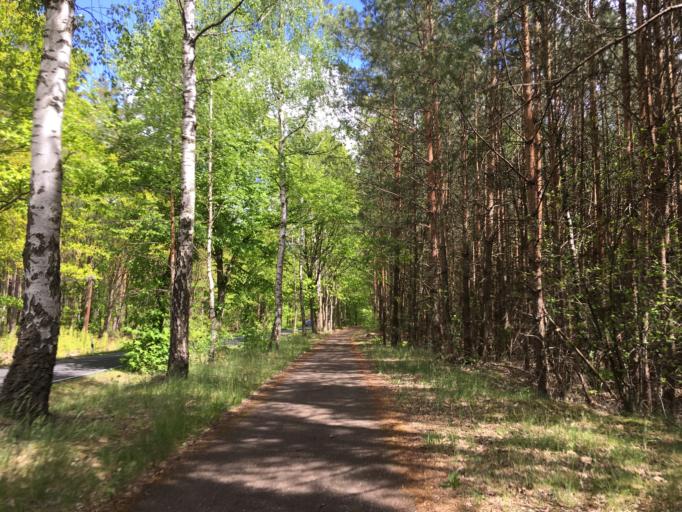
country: DE
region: Brandenburg
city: Liebenwalde
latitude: 52.8946
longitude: 13.5016
